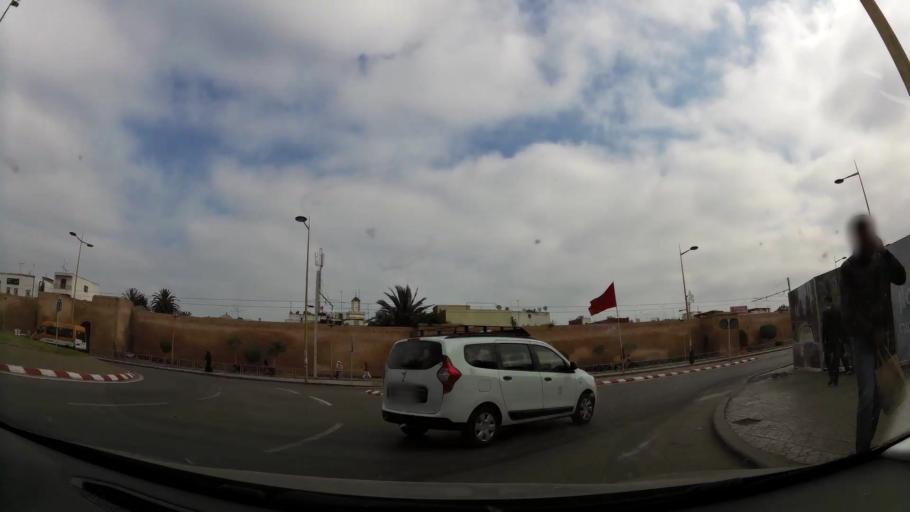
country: MA
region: Rabat-Sale-Zemmour-Zaer
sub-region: Rabat
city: Rabat
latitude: 34.0224
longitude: -6.8365
